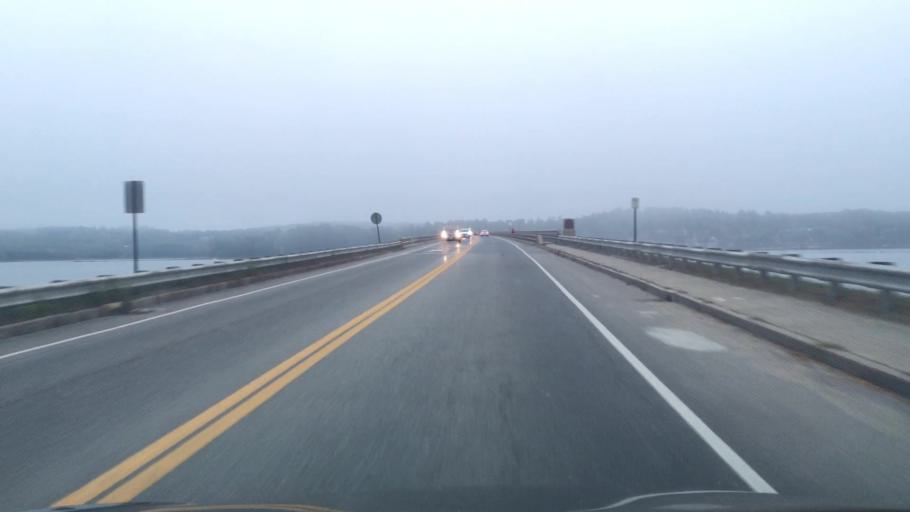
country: US
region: Maine
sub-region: Lincoln County
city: Wiscasset
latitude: 44.0021
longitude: -69.6633
